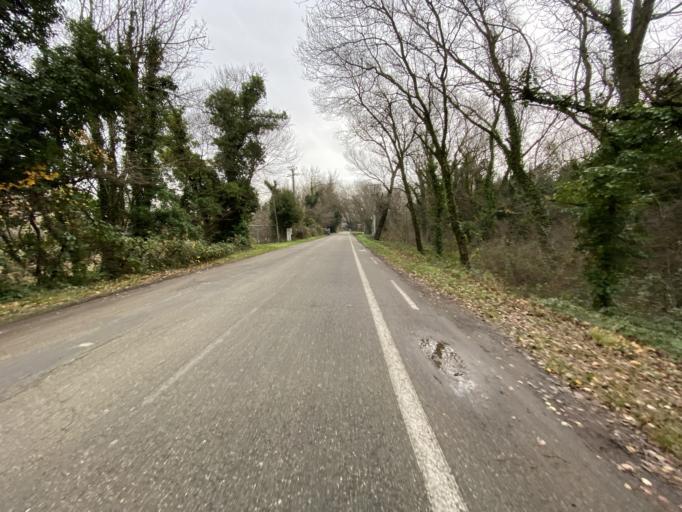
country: FR
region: Provence-Alpes-Cote d'Azur
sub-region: Departement du Vaucluse
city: Avignon
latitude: 43.9560
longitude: 4.8115
